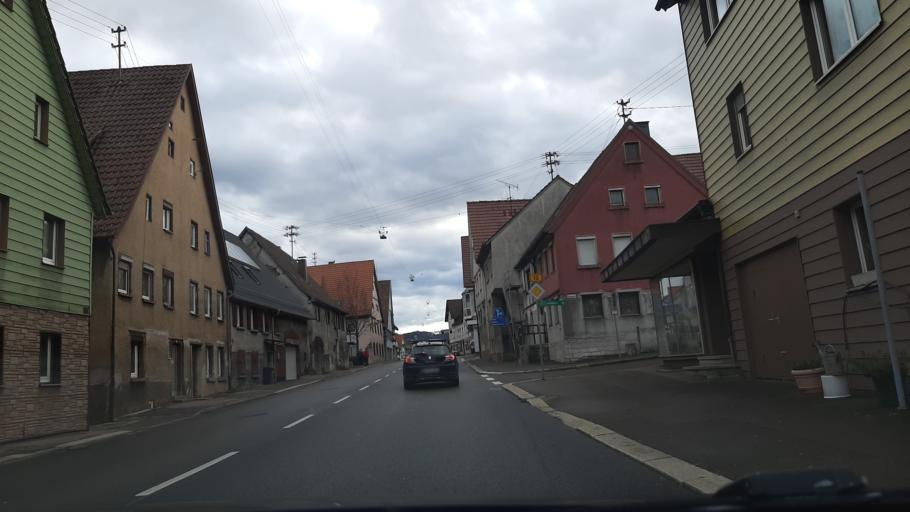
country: DE
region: Baden-Wuerttemberg
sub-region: Regierungsbezirk Stuttgart
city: Kuchen
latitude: 48.6369
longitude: 9.7976
